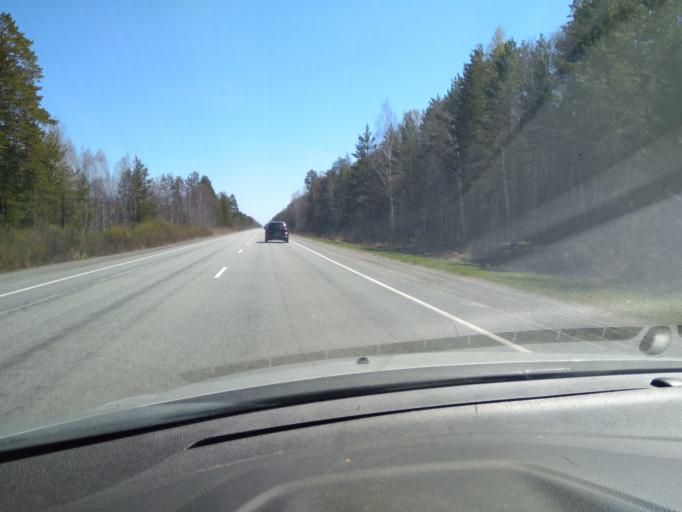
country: RU
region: Sverdlovsk
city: Yushala
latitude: 57.1131
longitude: 64.2548
